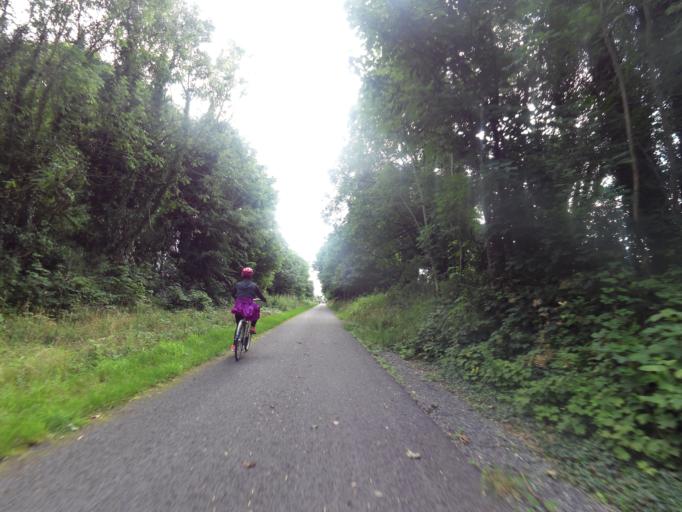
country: IE
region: Leinster
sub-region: An Iarmhi
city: Kilbeggan
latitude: 53.4648
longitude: -7.5033
